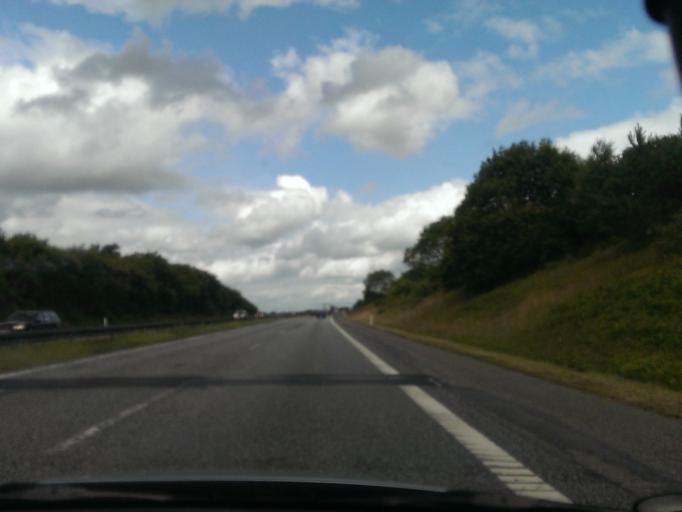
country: DK
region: North Denmark
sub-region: Mariagerfjord Kommune
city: Hobro
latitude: 56.5852
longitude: 9.7842
